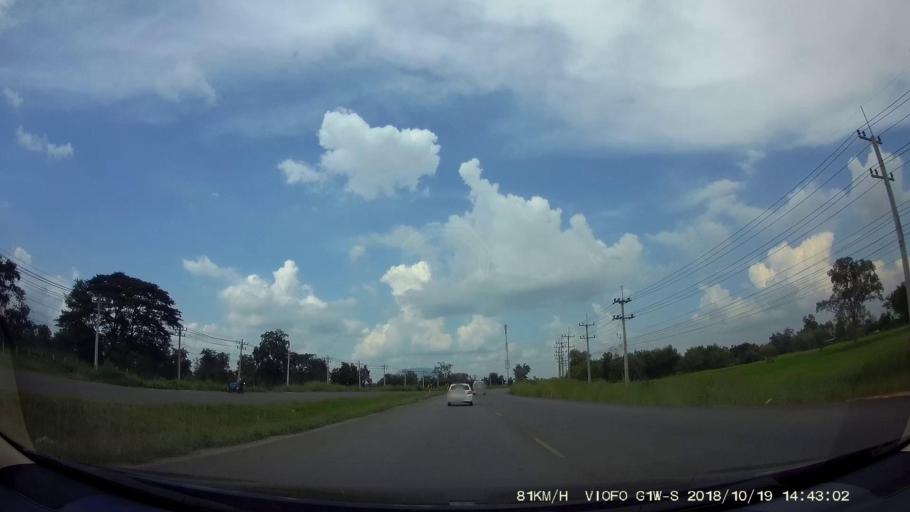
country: TH
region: Chaiyaphum
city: Phu Khiao
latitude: 16.2755
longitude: 102.2045
